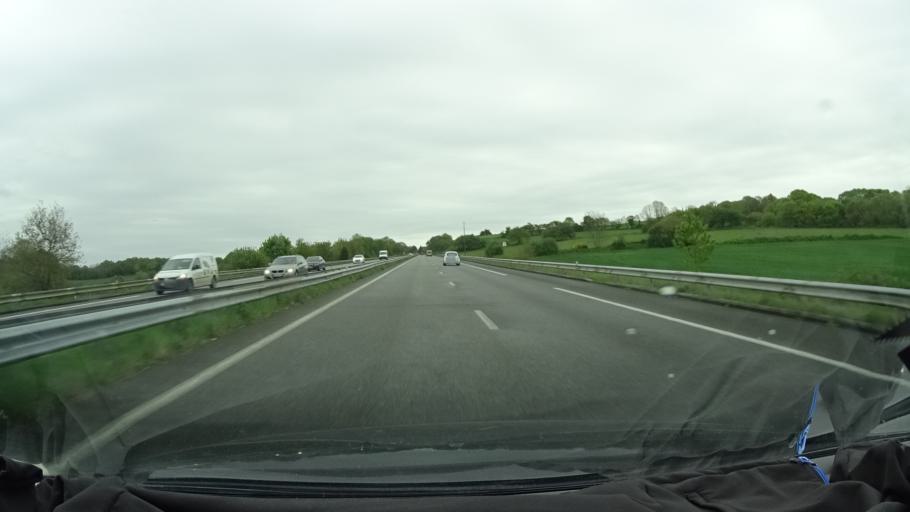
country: FR
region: Brittany
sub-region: Departement du Finistere
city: Le Faou
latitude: 48.2850
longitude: -4.1486
